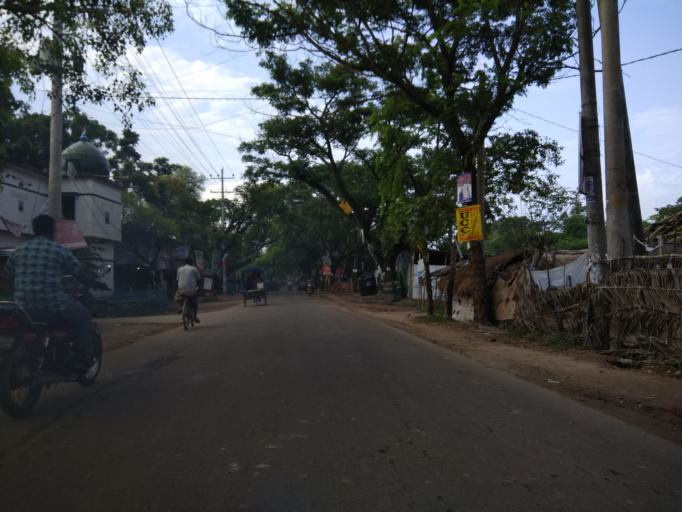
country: IN
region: West Bengal
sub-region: North 24 Parganas
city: Taki
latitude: 22.3394
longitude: 89.1059
